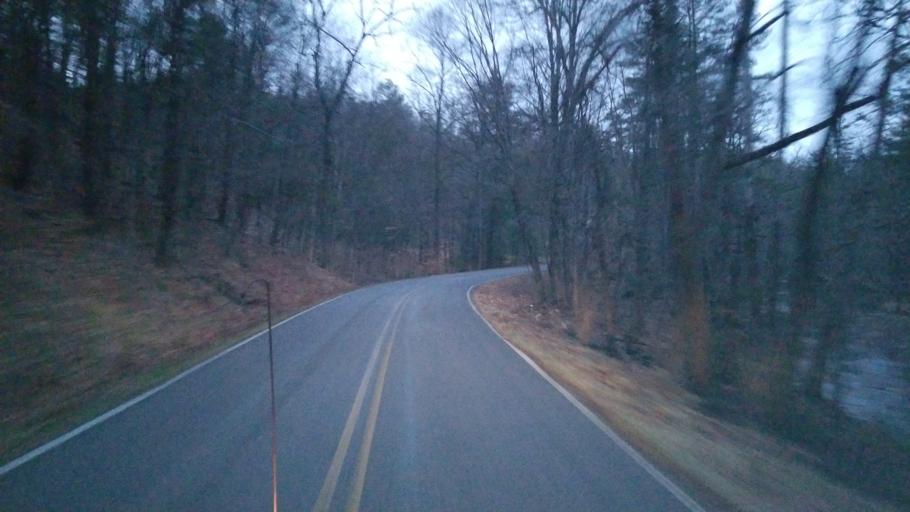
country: US
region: Virginia
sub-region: Pulaski County
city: Pulaski
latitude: 37.1326
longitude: -80.8589
